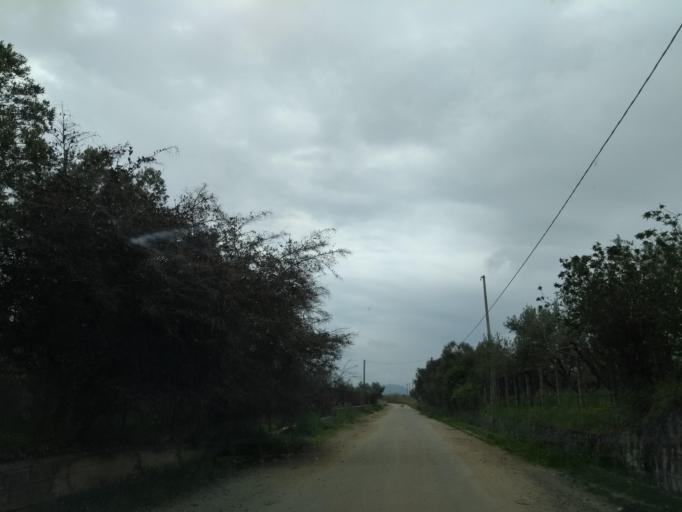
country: IT
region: Sicily
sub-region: Palermo
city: Partinico
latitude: 37.9927
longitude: 13.0751
